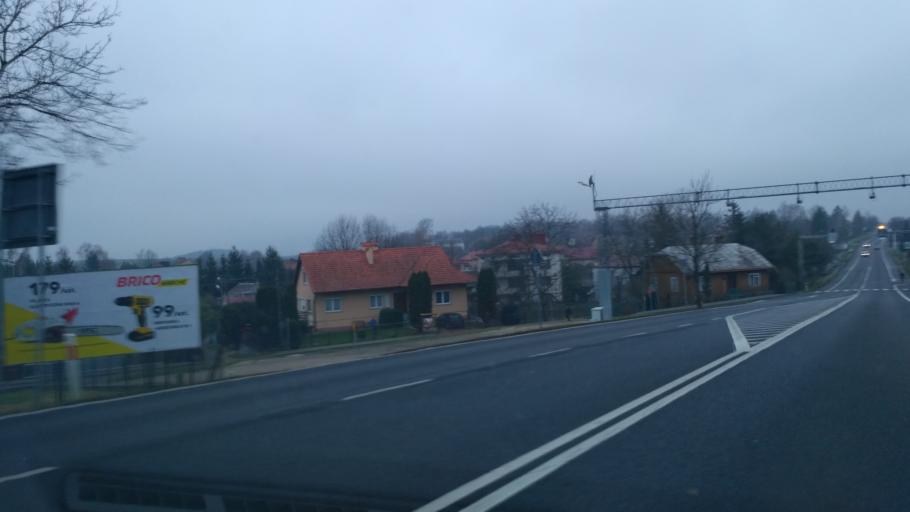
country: PL
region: Subcarpathian Voivodeship
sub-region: Powiat przeworski
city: Mirocin
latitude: 50.0416
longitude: 22.5576
